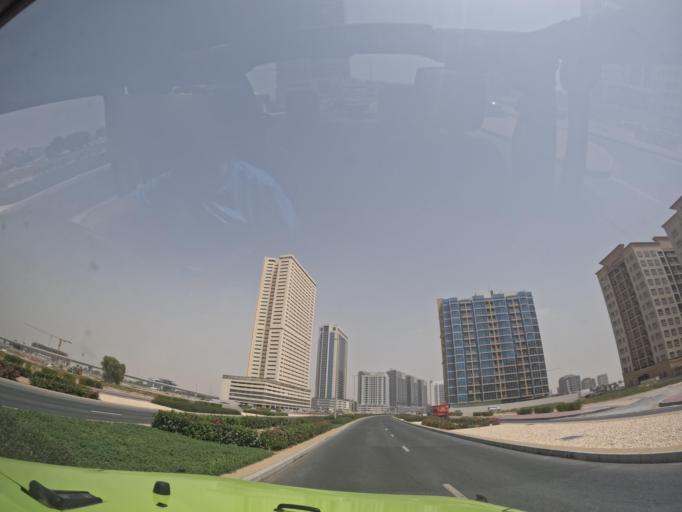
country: AE
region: Dubai
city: Dubai
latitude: 25.0963
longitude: 55.3803
